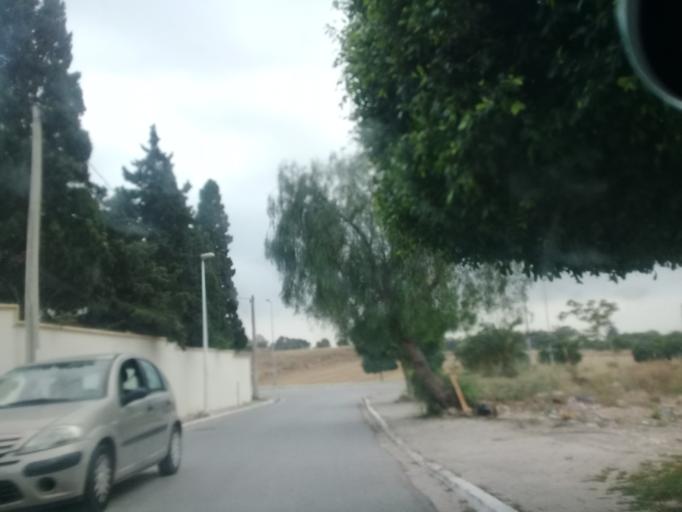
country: TN
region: Tunis
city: Sidi Bou Said
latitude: 36.8691
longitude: 10.3355
